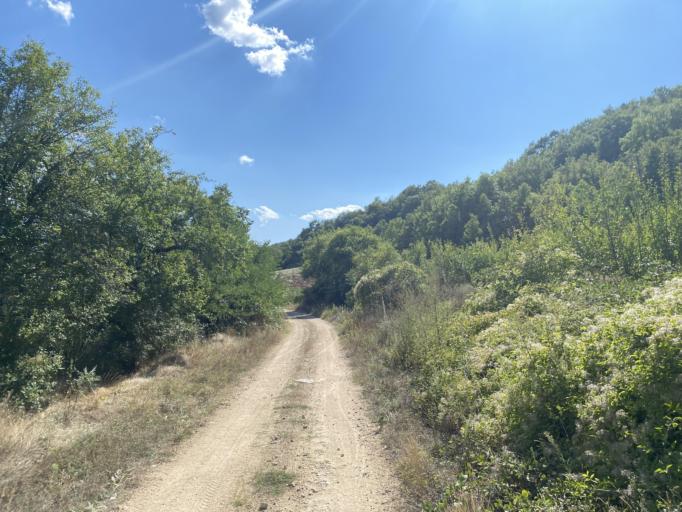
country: MK
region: Delcevo
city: Delcevo
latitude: 41.9032
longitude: 22.8064
